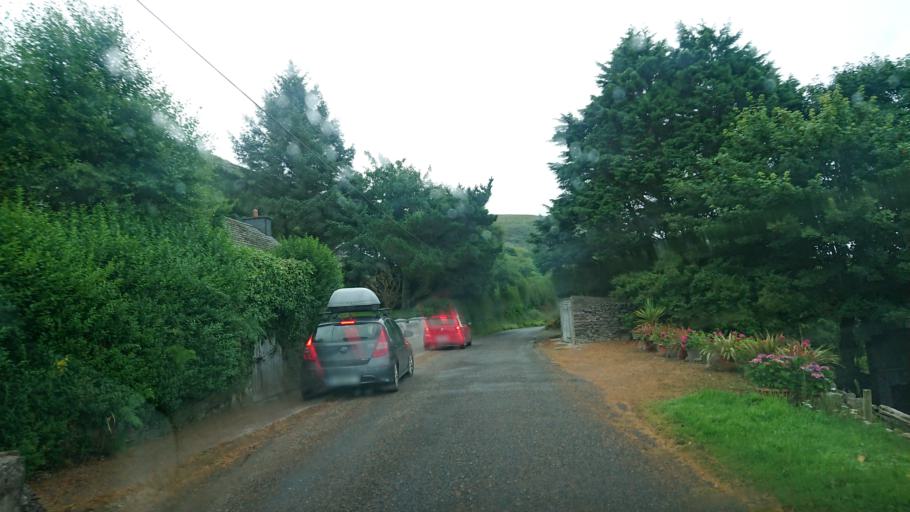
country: IE
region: Munster
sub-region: Ciarrai
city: Cahersiveen
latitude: 52.0234
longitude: -10.0939
